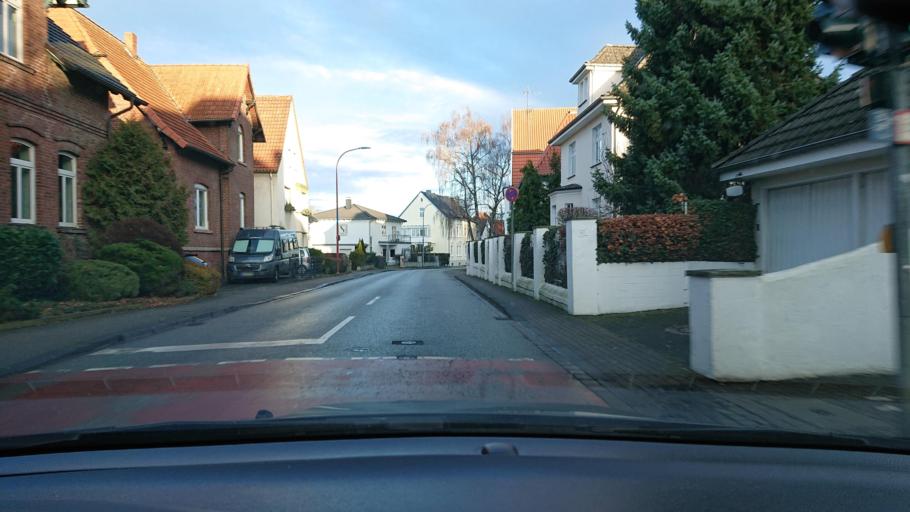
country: DE
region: North Rhine-Westphalia
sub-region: Regierungsbezirk Arnsberg
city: Soest
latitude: 51.5706
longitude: 8.0995
